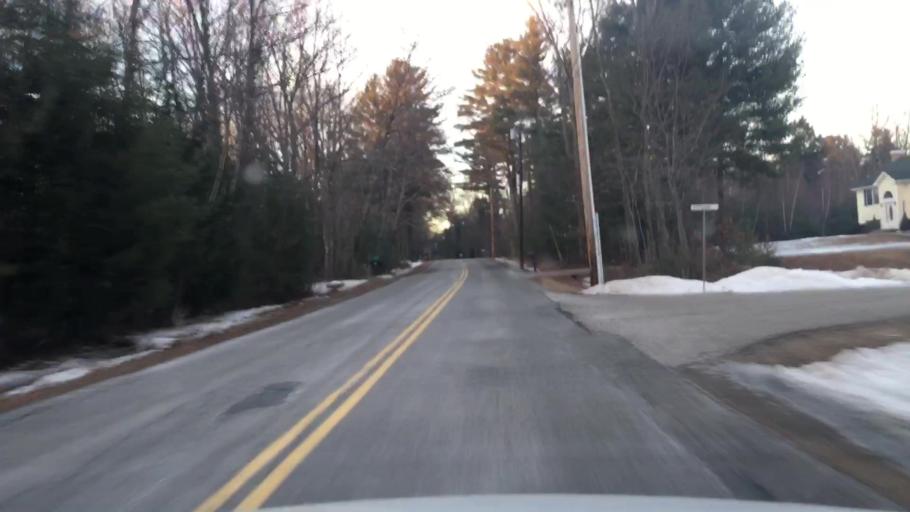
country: US
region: Maine
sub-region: York County
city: Lebanon
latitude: 43.3329
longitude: -70.8638
